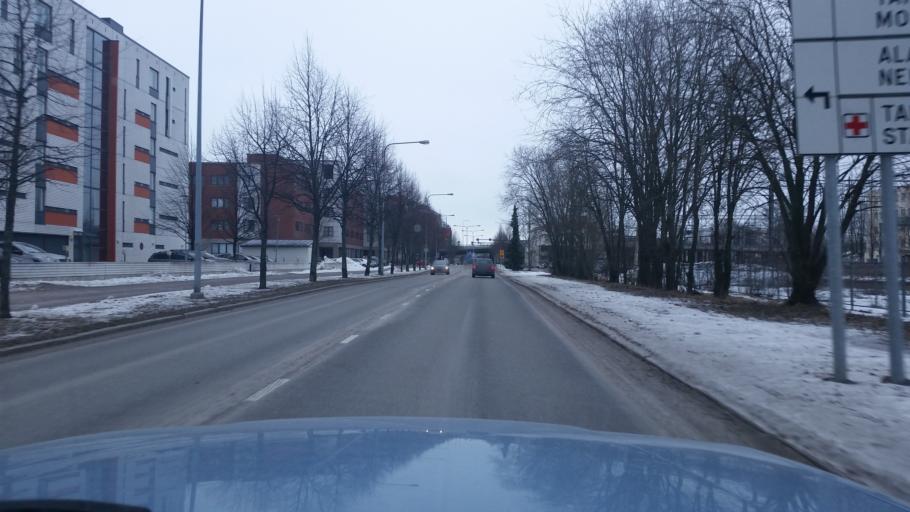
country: FI
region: Uusimaa
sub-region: Helsinki
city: Vantaa
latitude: 60.2486
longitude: 25.0049
